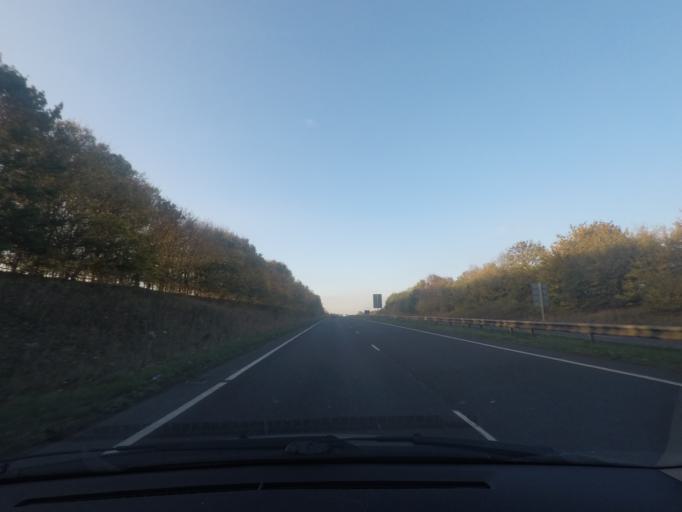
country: GB
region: England
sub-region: North Lincolnshire
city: Barnetby le Wold
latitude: 53.5929
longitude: -0.4179
